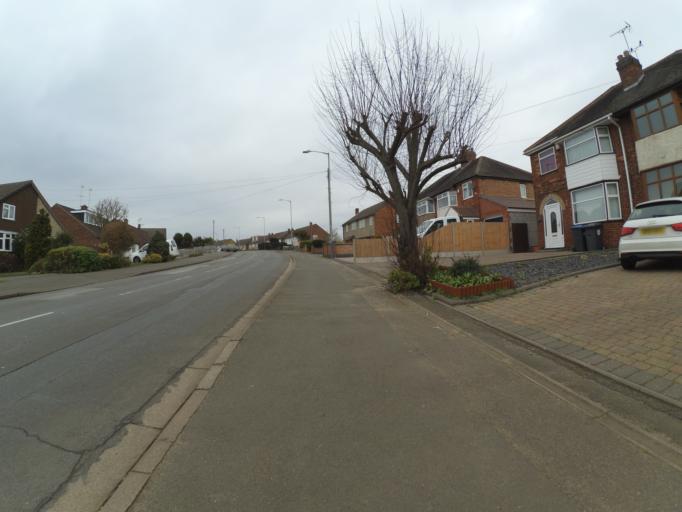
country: GB
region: England
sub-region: Warwickshire
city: Rugby
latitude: 52.3649
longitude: -1.2188
